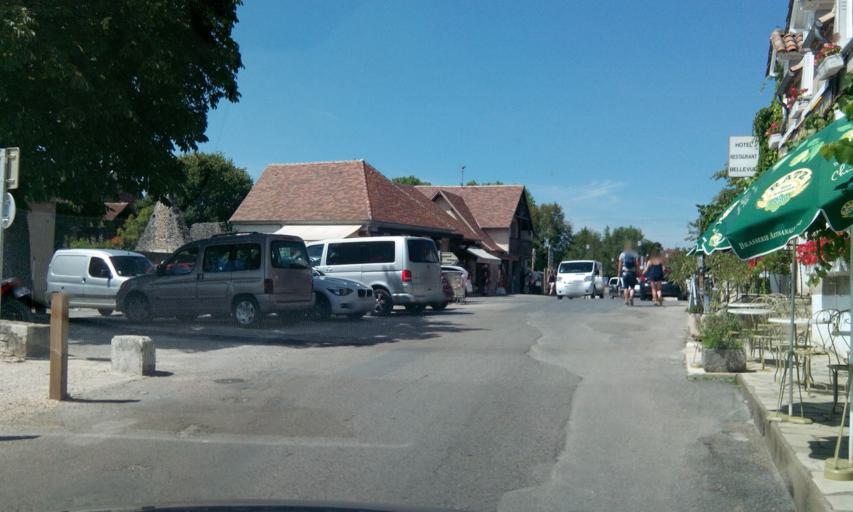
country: FR
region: Midi-Pyrenees
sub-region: Departement du Lot
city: Gramat
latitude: 44.8037
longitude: 1.6272
